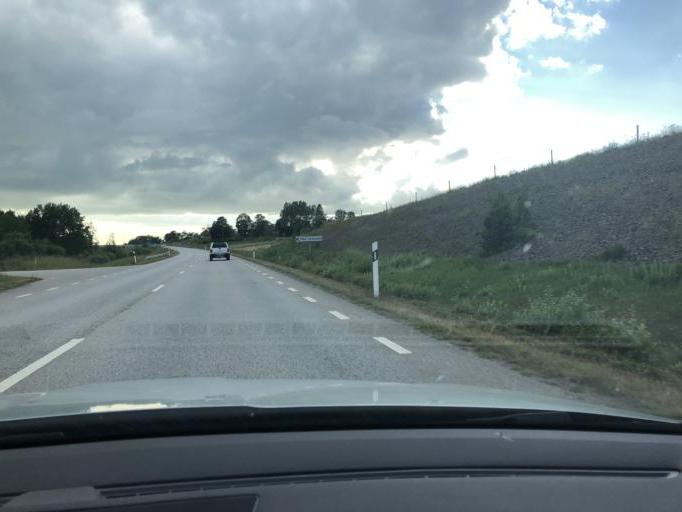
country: SE
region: Skane
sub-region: Simrishamns Kommun
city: Simrishamn
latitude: 55.5358
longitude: 14.2923
